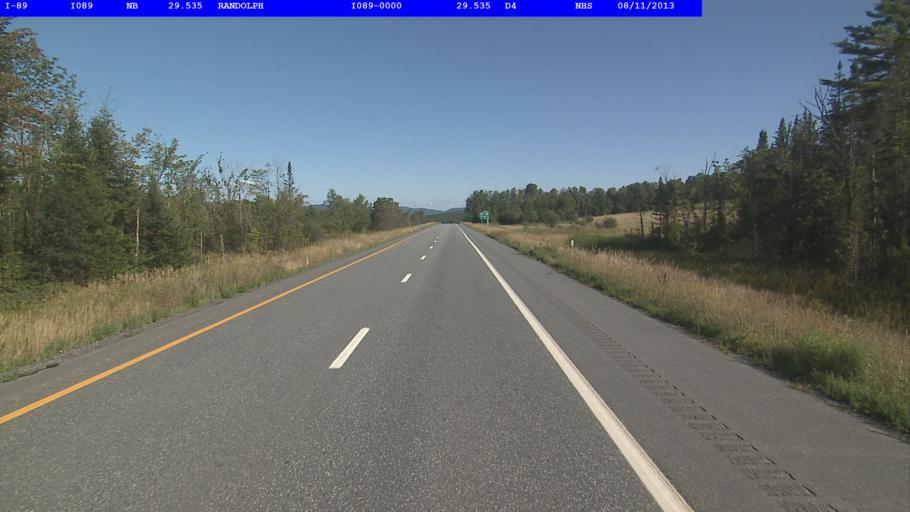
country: US
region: Vermont
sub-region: Orange County
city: Randolph
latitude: 43.9255
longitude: -72.6158
